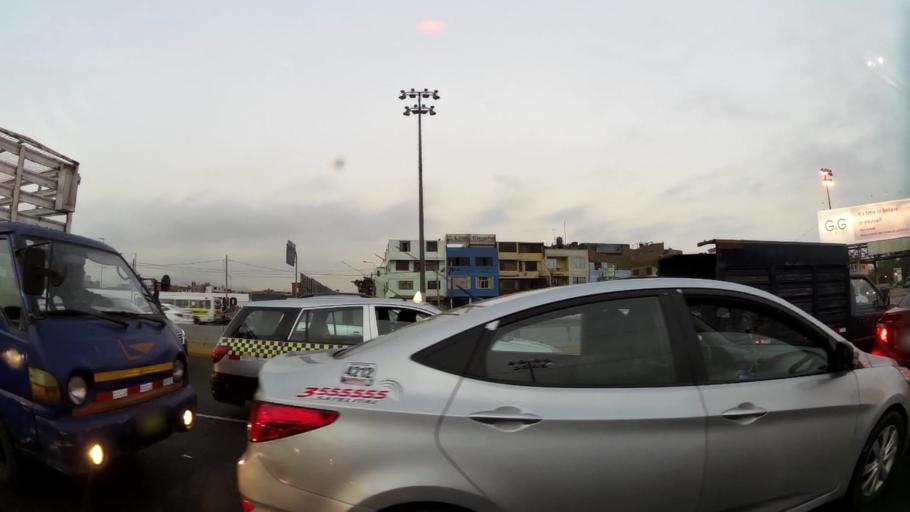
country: PE
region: Callao
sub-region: Callao
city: Callao
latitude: -12.0370
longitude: -77.0995
